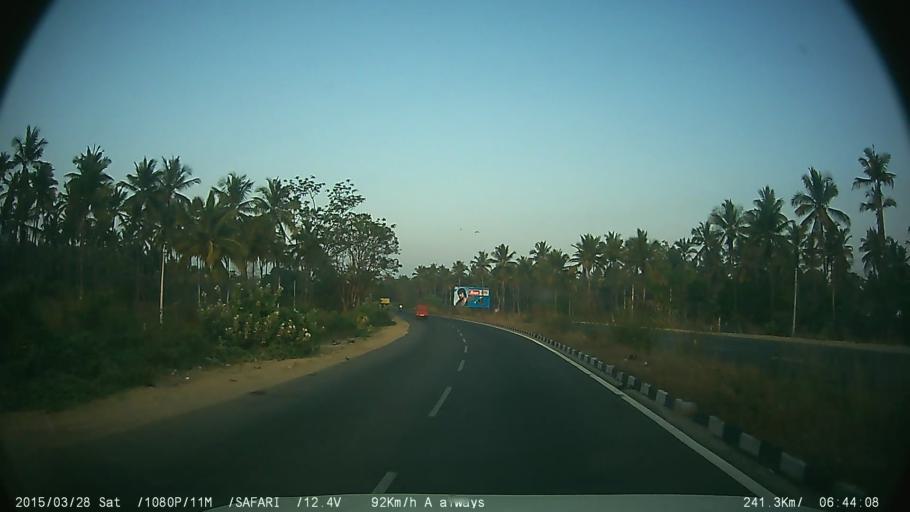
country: IN
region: Karnataka
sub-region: Mandya
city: Maddur
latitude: 12.6287
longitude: 77.1100
